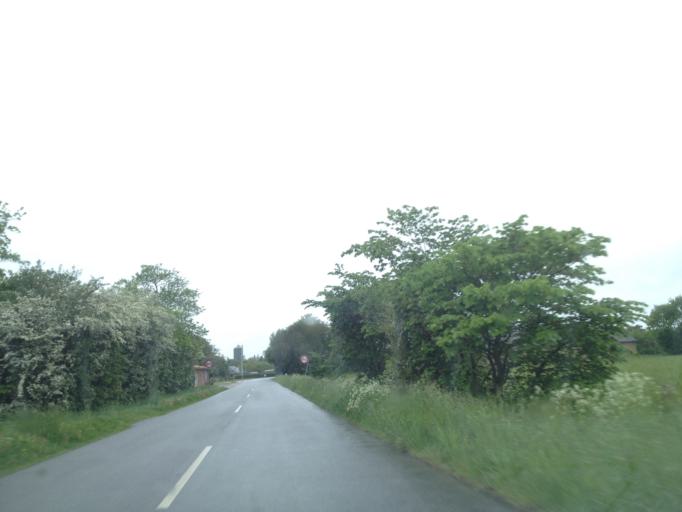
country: DK
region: South Denmark
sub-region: Tonder Kommune
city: Sherrebek
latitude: 55.1193
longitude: 8.7599
